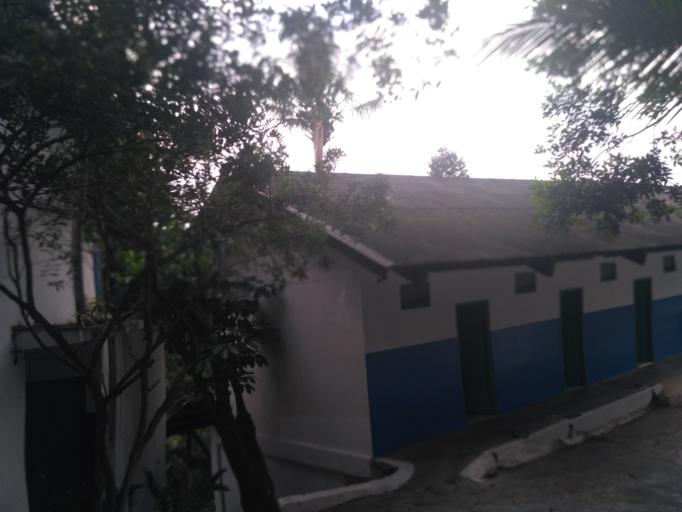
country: ID
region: Central Java
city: Ungaran
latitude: -7.0714
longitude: 110.4386
